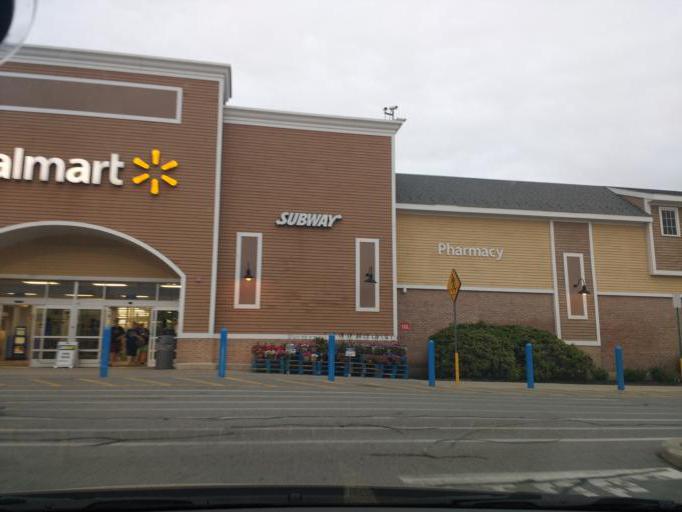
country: US
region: Massachusetts
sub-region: Barnstable County
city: Teaticket
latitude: 41.5608
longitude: -70.5947
